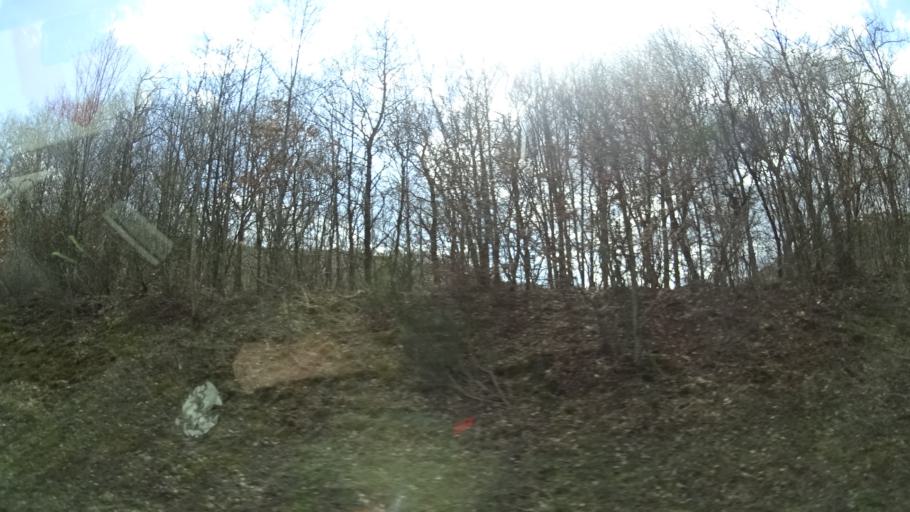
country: DE
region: Rheinland-Pfalz
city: Gerach
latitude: 49.7580
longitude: 7.3403
